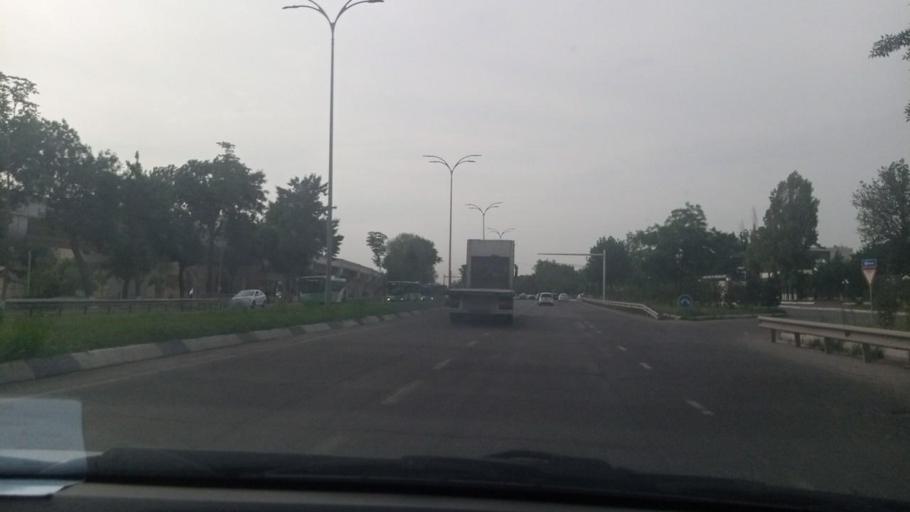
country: UZ
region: Toshkent
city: Salor
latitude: 41.2950
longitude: 69.3542
